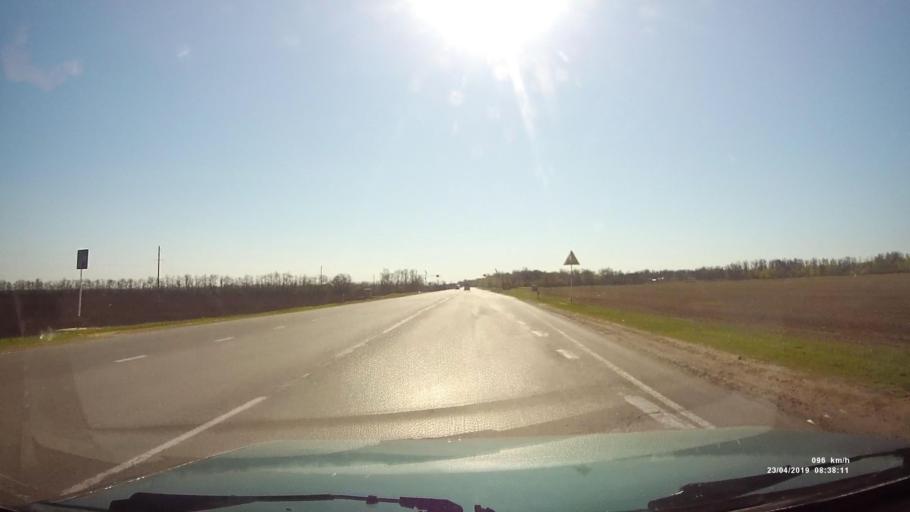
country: RU
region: Rostov
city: Tselina
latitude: 46.5313
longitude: 41.1829
